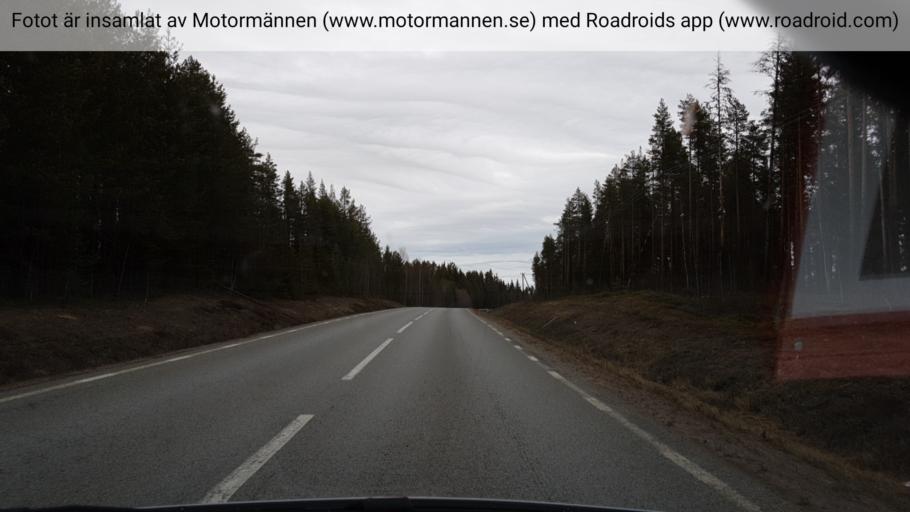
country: SE
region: Vaesterbotten
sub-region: Asele Kommun
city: Asele
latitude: 63.7776
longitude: 17.0252
